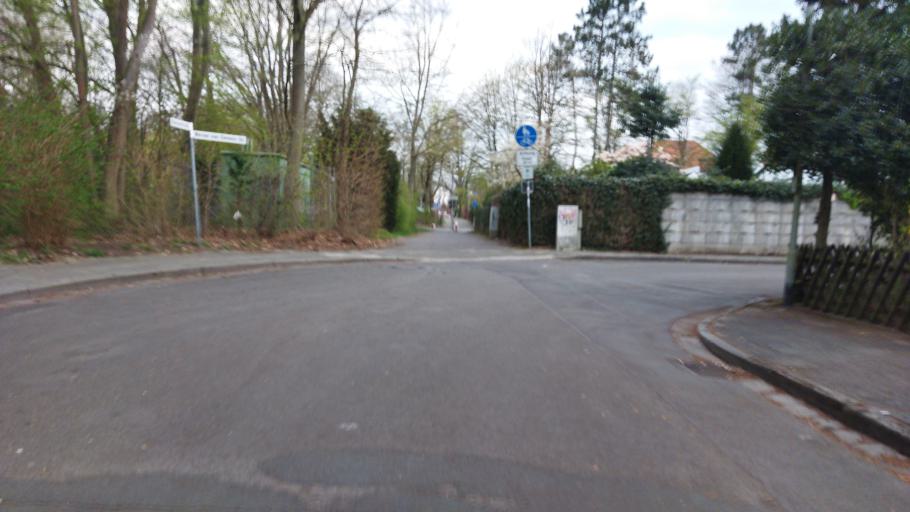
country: DE
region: Lower Saxony
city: Nienburg
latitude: 52.6224
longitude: 9.2081
